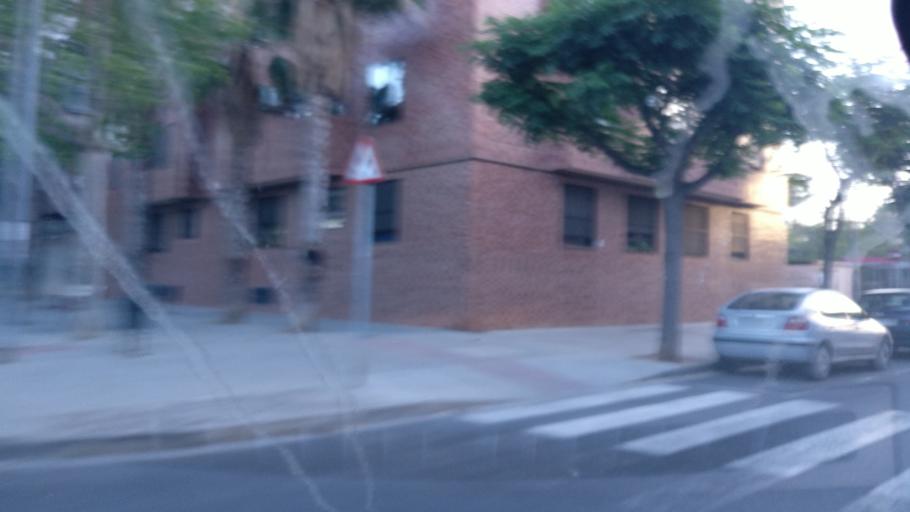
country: ES
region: Valencia
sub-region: Provincia de Valencia
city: Aldaia
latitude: 39.4629
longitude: -0.4570
